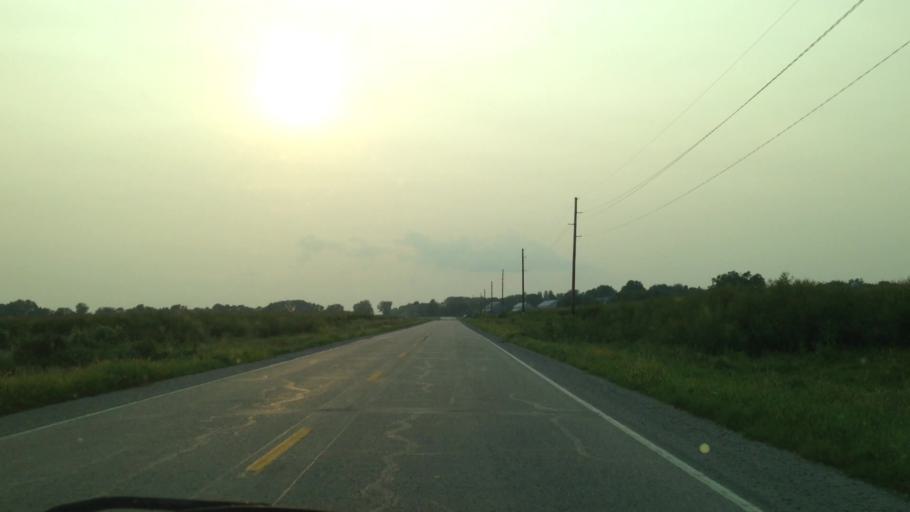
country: US
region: Iowa
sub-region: Iowa County
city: Marengo
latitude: 41.8038
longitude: -91.9529
